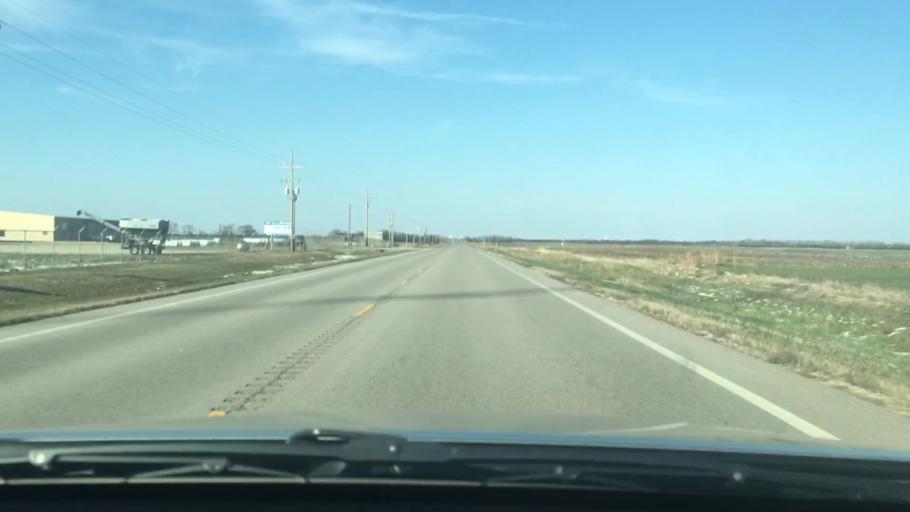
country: US
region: Kansas
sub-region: Rice County
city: Sterling
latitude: 38.2764
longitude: -98.2020
